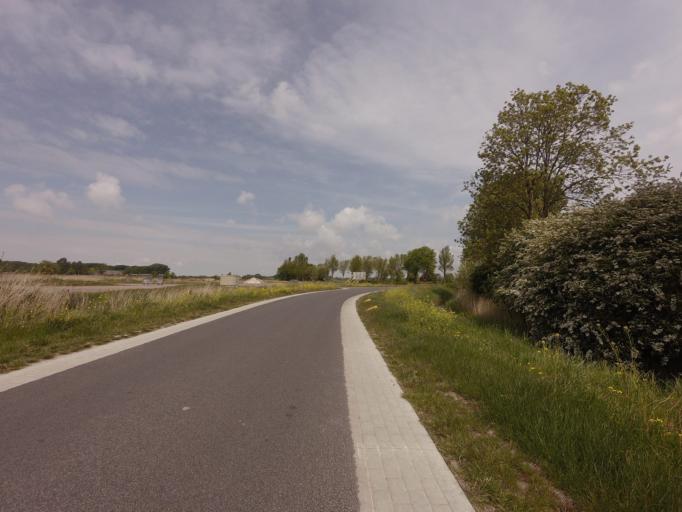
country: NL
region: Friesland
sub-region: Sudwest Fryslan
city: Bolsward
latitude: 53.0990
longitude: 5.4791
